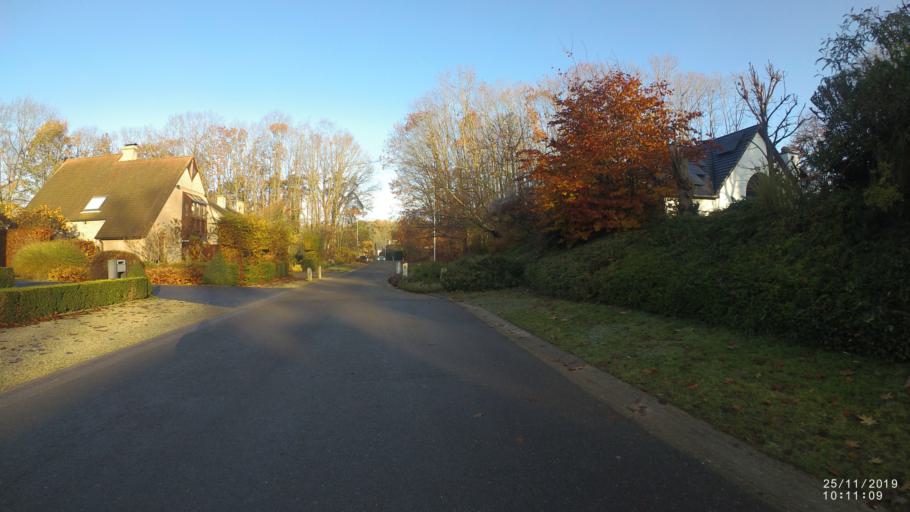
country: BE
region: Flanders
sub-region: Provincie Vlaams-Brabant
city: Diest
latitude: 50.9949
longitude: 5.0249
